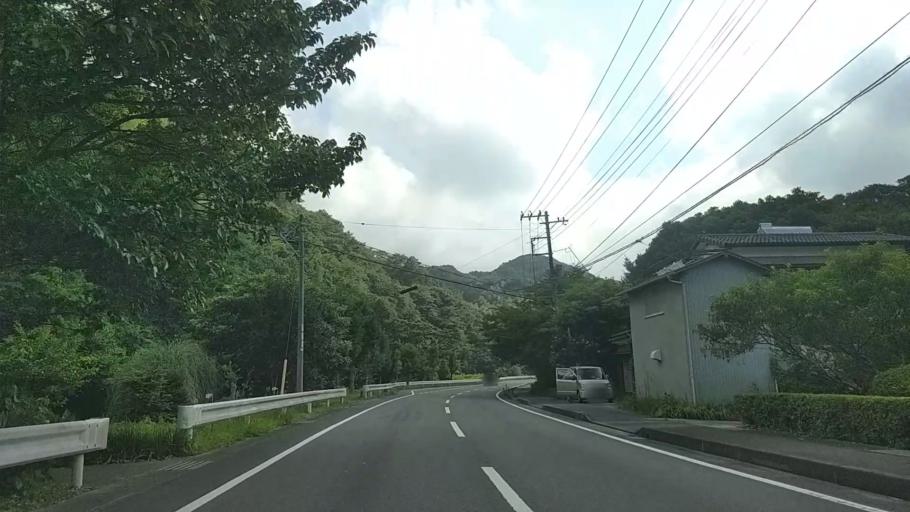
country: JP
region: Shizuoka
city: Shimoda
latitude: 34.6531
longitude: 138.8337
